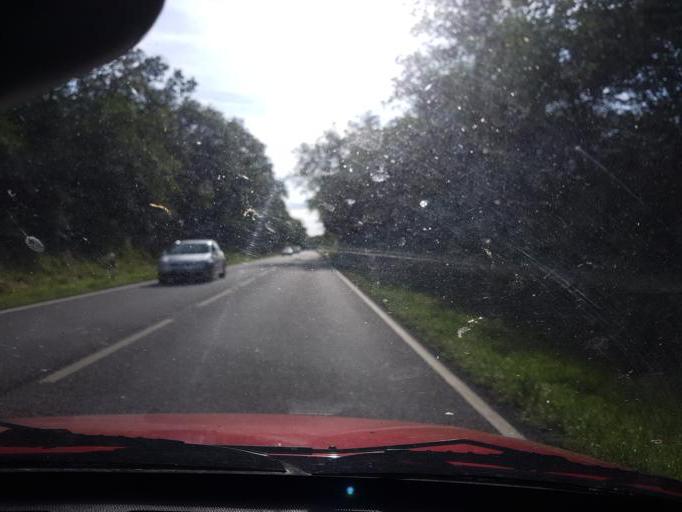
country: DE
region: Hesse
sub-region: Regierungsbezirk Giessen
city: Grossen Buseck
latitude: 50.5886
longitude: 8.7626
